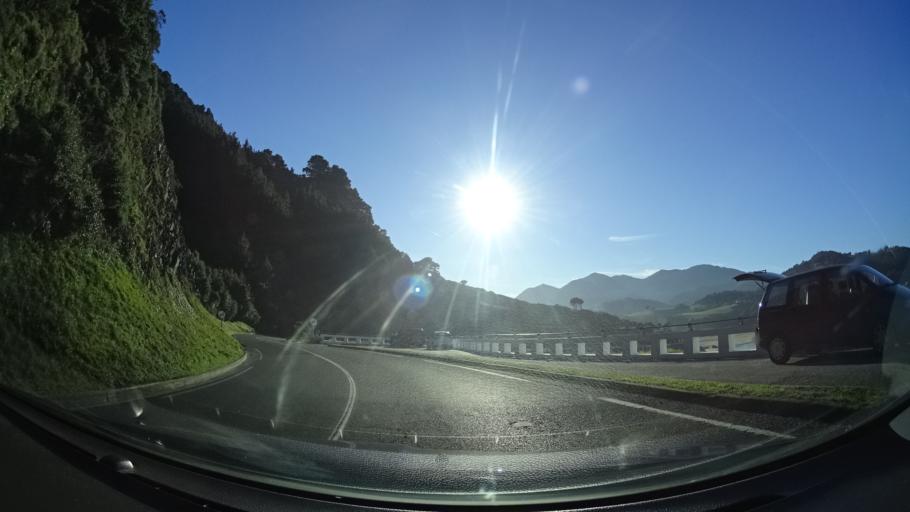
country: ES
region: Basque Country
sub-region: Provincia de Guipuzcoa
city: Deba
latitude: 43.2957
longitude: -2.3431
